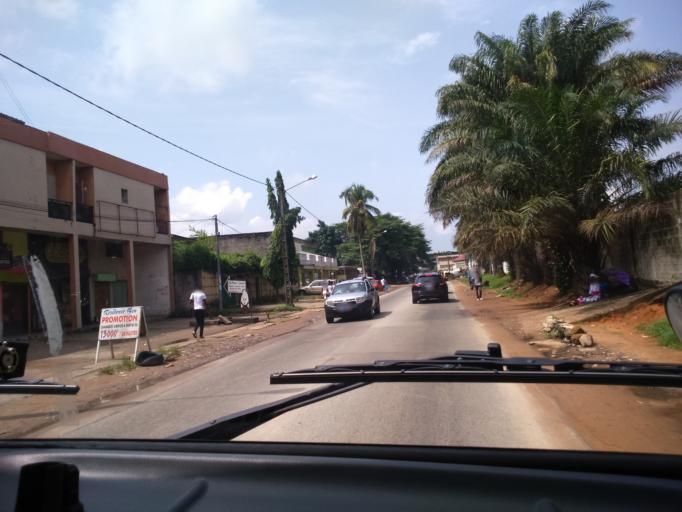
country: CI
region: Lagunes
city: Abidjan
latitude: 5.3587
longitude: -3.9784
